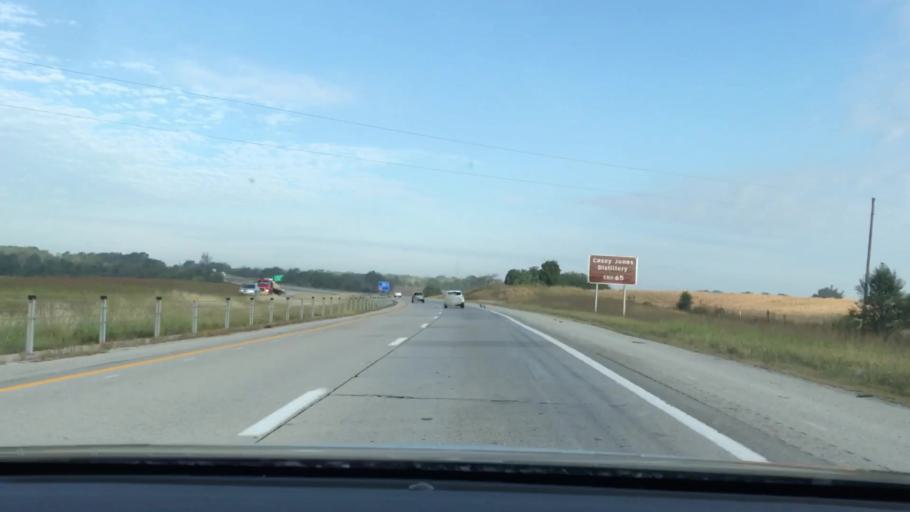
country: US
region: Kentucky
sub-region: Trigg County
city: Cadiz
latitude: 36.8677
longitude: -87.7120
